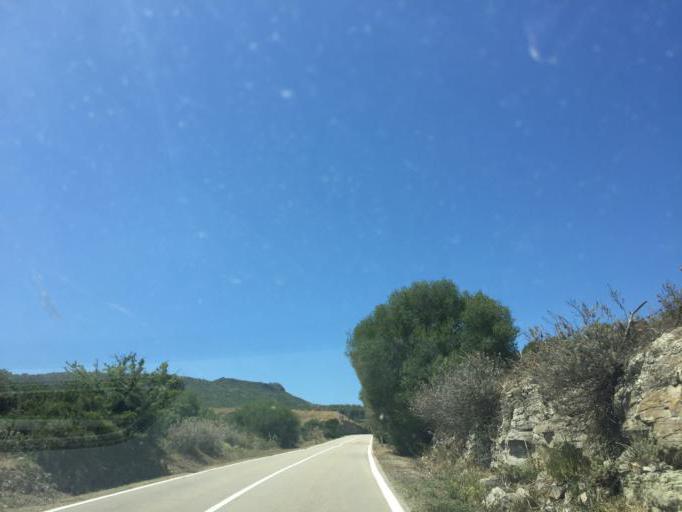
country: IT
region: Sardinia
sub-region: Provincia di Sassari
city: Castelsardo
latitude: 40.8946
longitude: 8.7564
